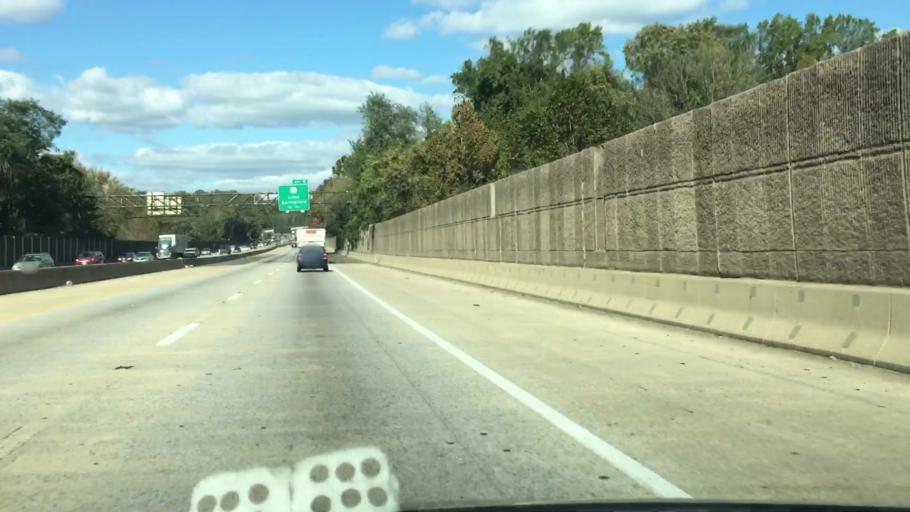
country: US
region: Pennsylvania
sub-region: Delaware County
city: Swarthmore
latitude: 39.9213
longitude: -75.3622
